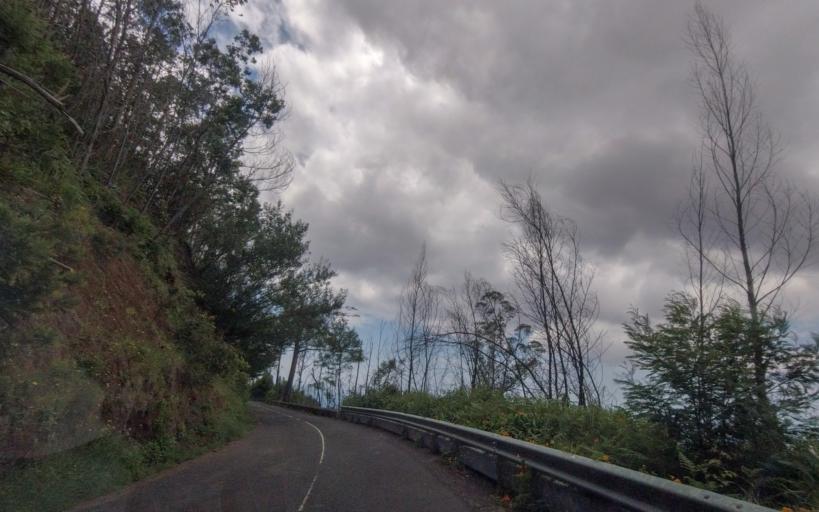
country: PT
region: Madeira
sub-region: Funchal
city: Nossa Senhora do Monte
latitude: 32.6750
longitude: -16.8844
